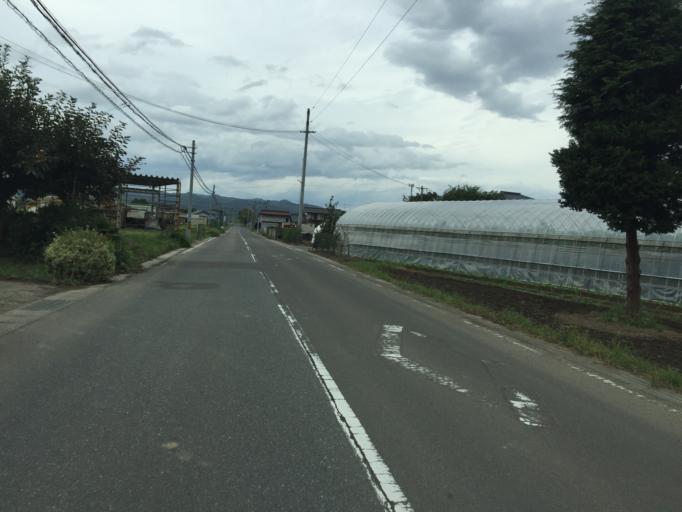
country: JP
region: Fukushima
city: Yanagawamachi-saiwaicho
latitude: 37.8544
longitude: 140.5882
